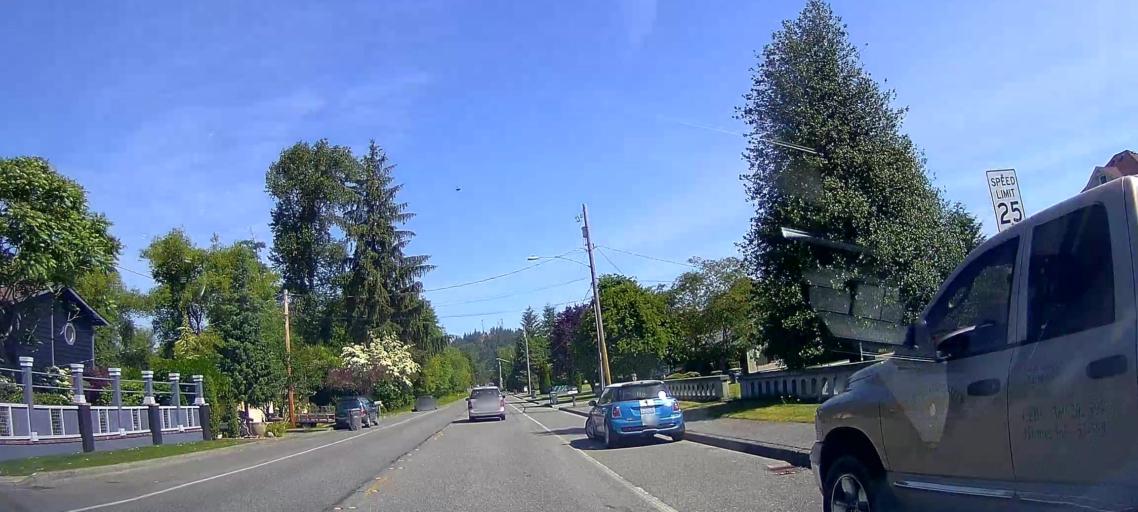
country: US
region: Washington
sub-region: Skagit County
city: Burlington
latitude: 48.4667
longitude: -122.3248
